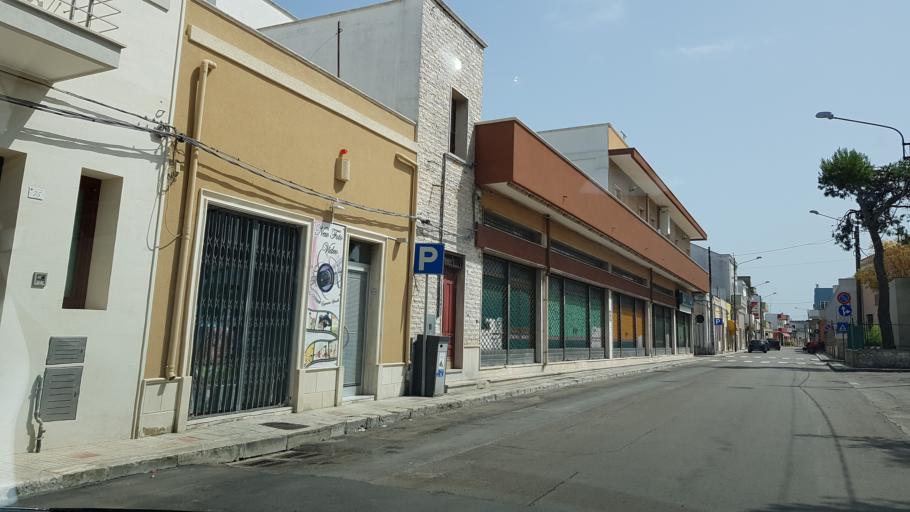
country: IT
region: Apulia
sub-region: Provincia di Brindisi
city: San Pancrazio Salentino
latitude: 40.4162
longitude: 17.8397
